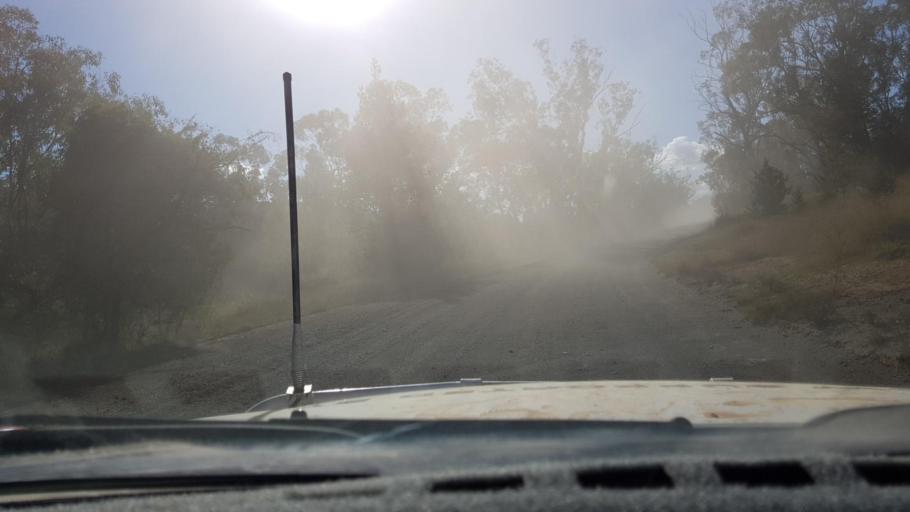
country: AU
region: New South Wales
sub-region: Narrabri
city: Blair Athol
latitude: -30.6654
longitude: 150.3459
